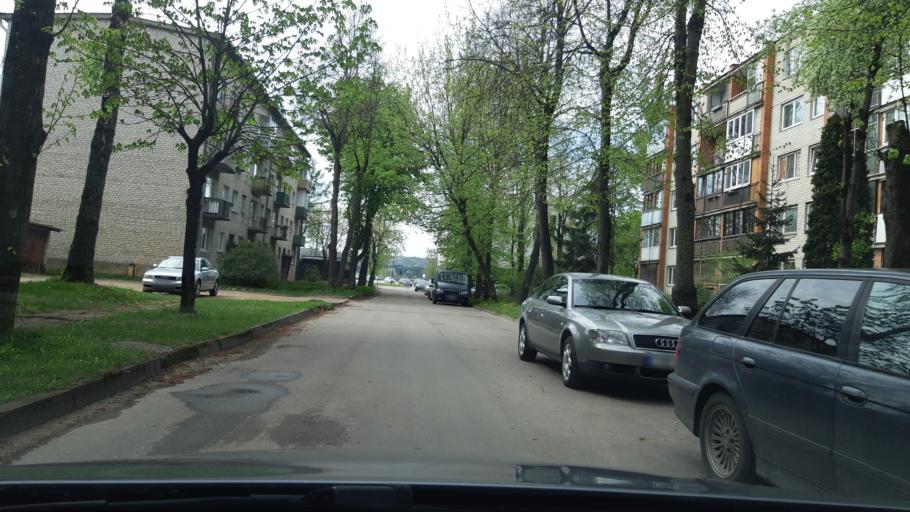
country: LT
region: Kauno apskritis
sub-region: Kauno rajonas
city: Akademija (Kaunas)
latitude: 54.9172
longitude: 23.8372
